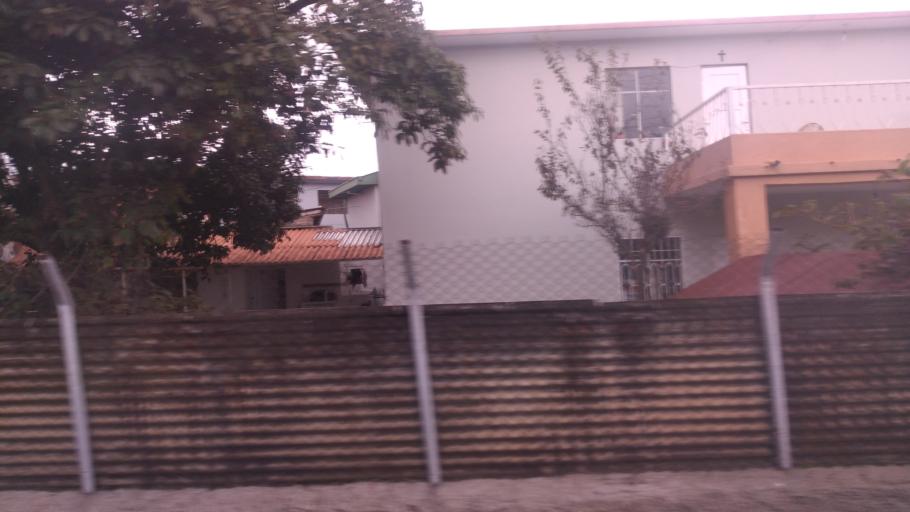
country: EC
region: Azuay
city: Cuenca
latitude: -2.8993
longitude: -79.0143
